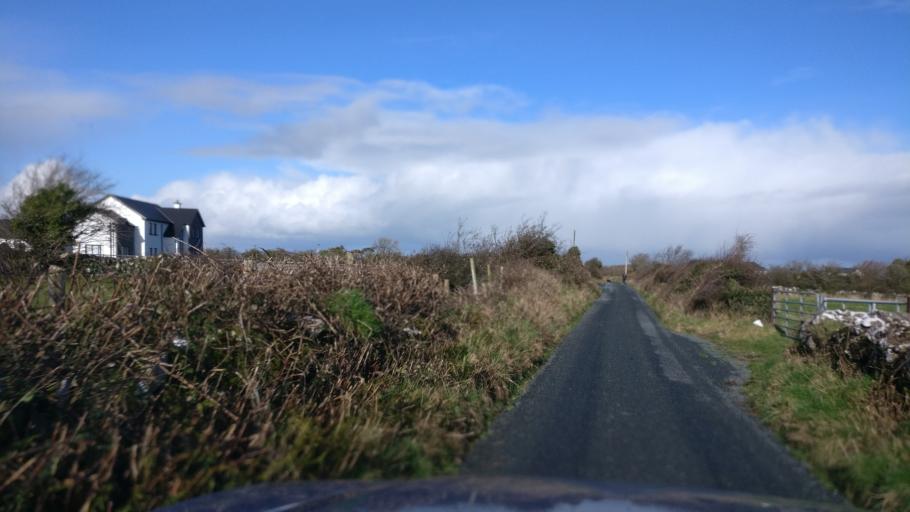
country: IE
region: Connaught
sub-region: County Galway
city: Athenry
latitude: 53.2392
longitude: -8.7748
